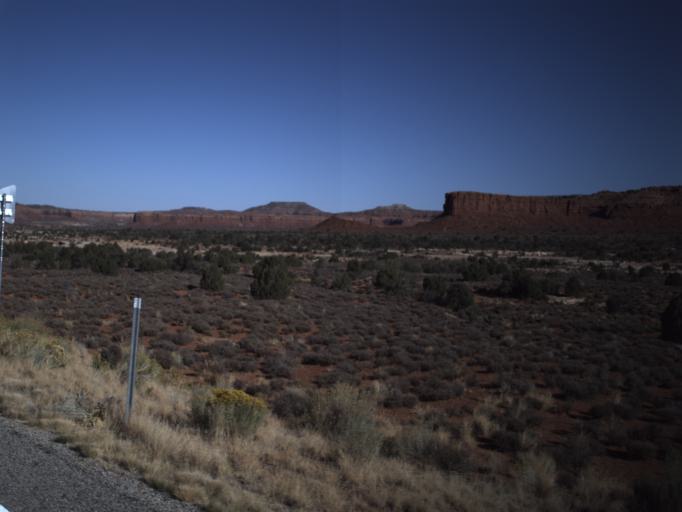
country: US
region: Utah
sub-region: San Juan County
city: Blanding
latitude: 37.6740
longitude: -110.2067
